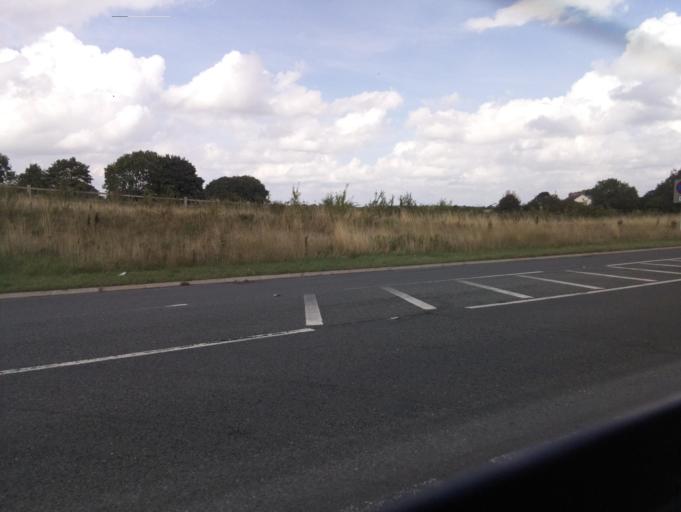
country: GB
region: England
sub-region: Darlington
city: High Coniscliffe
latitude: 54.4672
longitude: -1.6589
